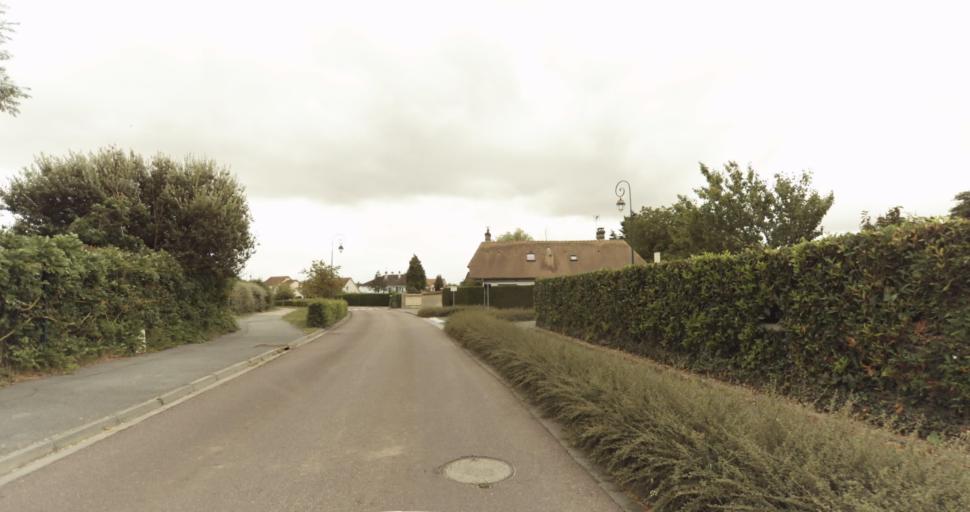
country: FR
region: Haute-Normandie
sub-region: Departement de l'Eure
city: Evreux
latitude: 48.9775
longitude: 1.1900
